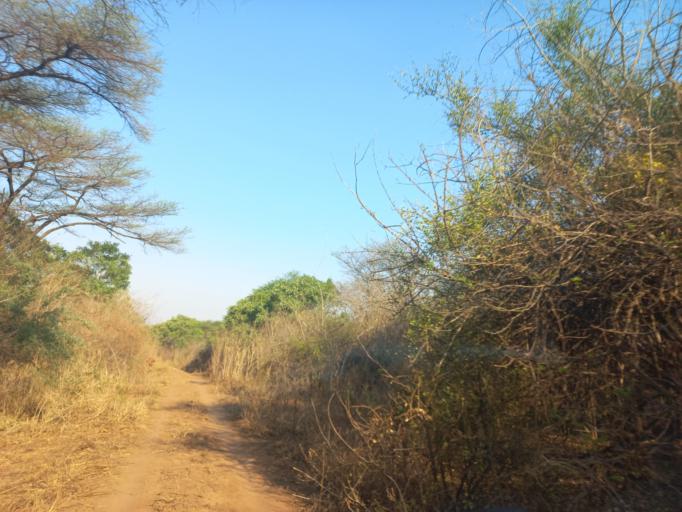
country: ZM
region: Lusaka
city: Luangwa
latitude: -15.4175
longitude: 30.2465
